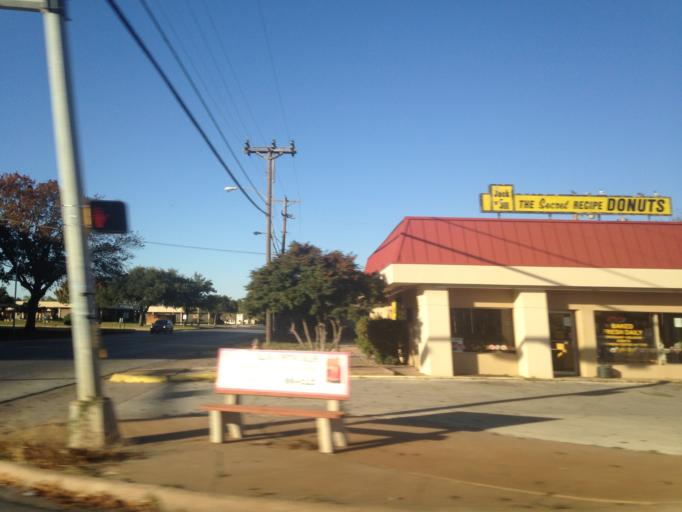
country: US
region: Texas
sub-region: Taylor County
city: Abilene
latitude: 32.4323
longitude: -99.7633
